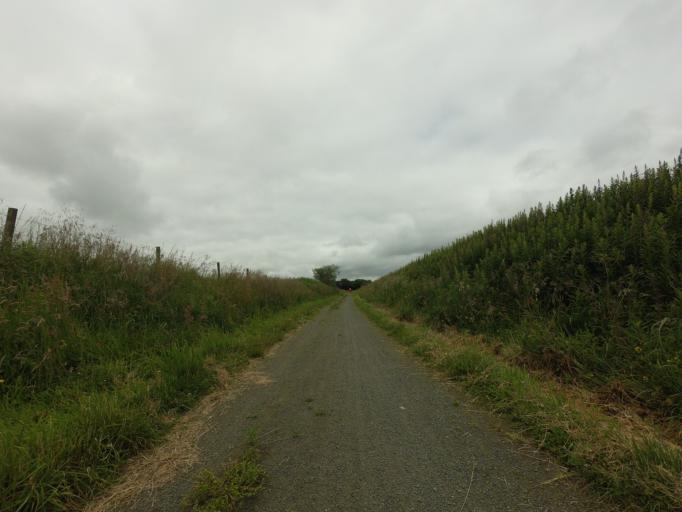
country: GB
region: Scotland
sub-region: Aberdeenshire
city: Ellon
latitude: 57.4848
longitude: -2.1351
